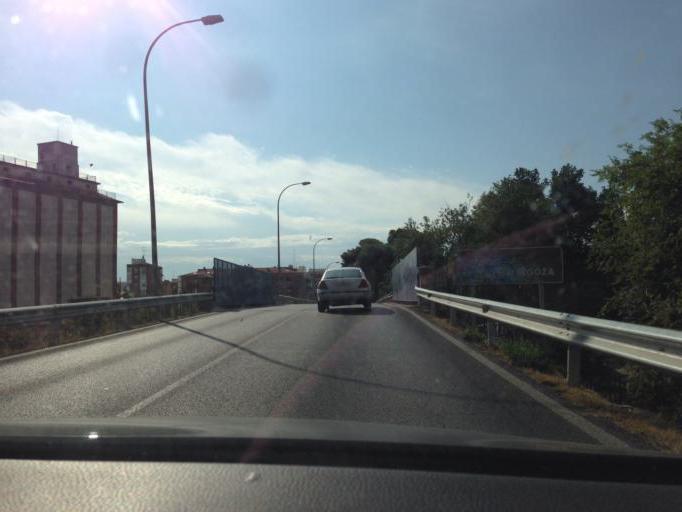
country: ES
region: Madrid
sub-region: Provincia de Madrid
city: Alcala de Henares
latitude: 40.4874
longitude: -3.3727
